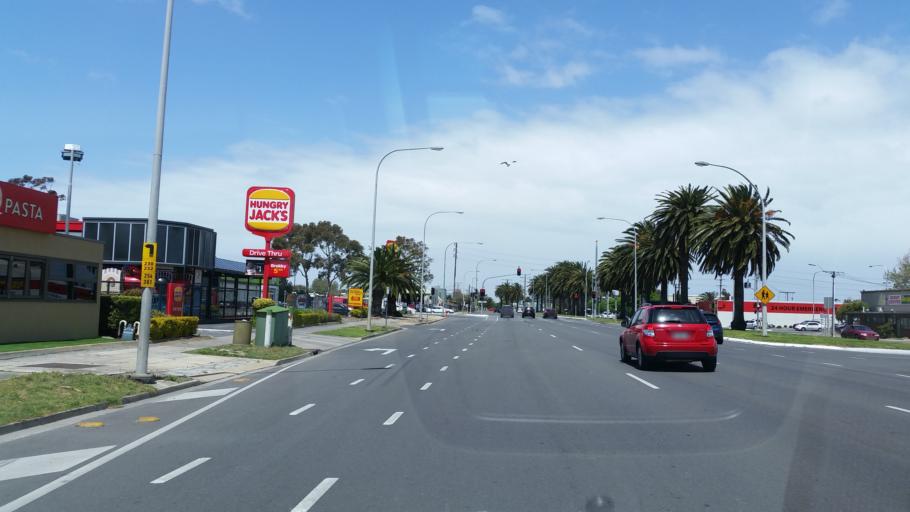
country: AU
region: South Australia
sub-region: Port Adelaide Enfield
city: Alberton
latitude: -34.8511
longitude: 138.5094
